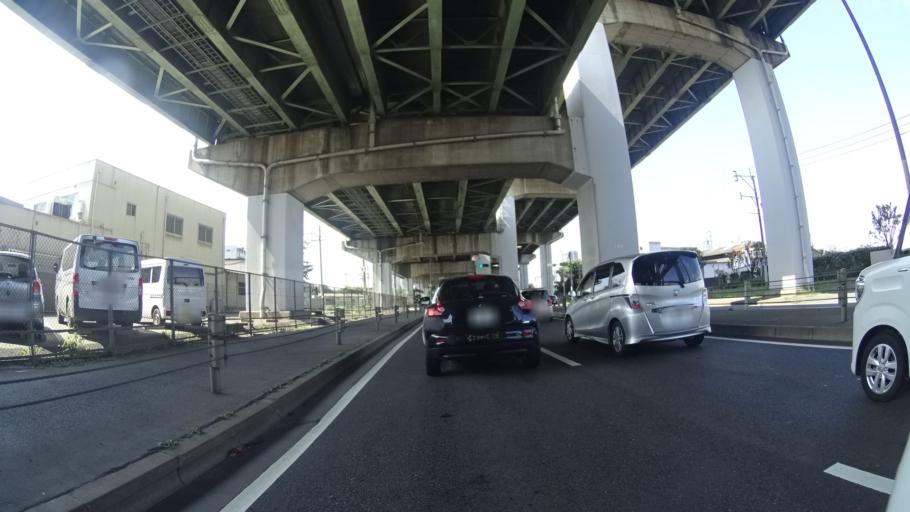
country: JP
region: Fukuoka
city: Kitakyushu
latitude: 33.8917
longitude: 130.8671
